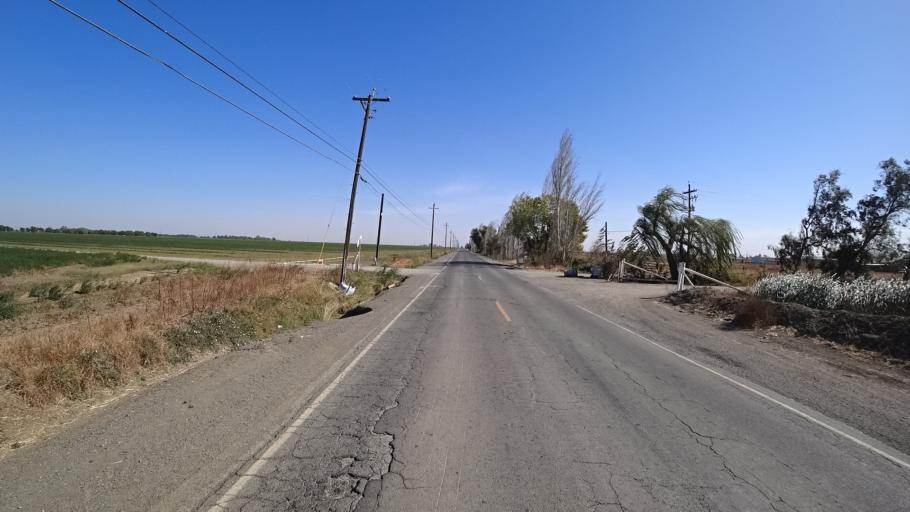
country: US
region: California
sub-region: Yolo County
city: Woodland
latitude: 38.6190
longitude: -121.7396
